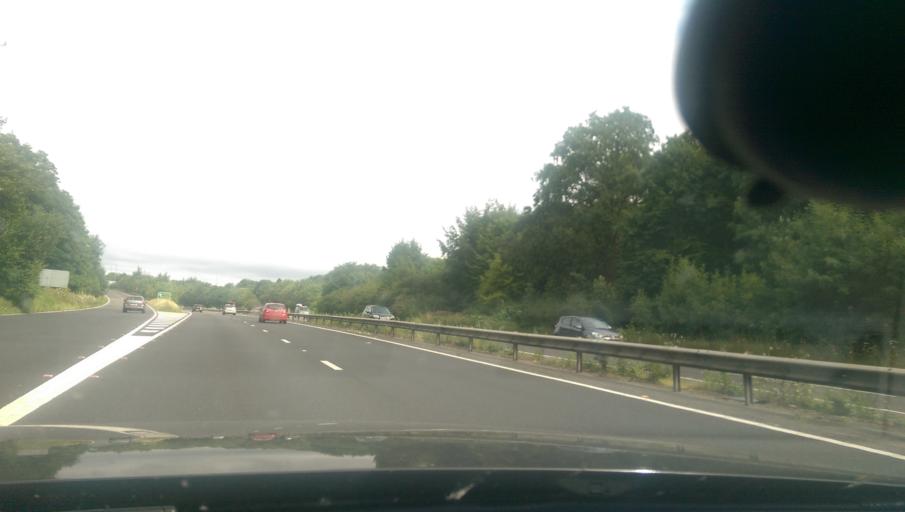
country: GB
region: England
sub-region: Hampshire
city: Andover
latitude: 51.2067
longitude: -1.5138
